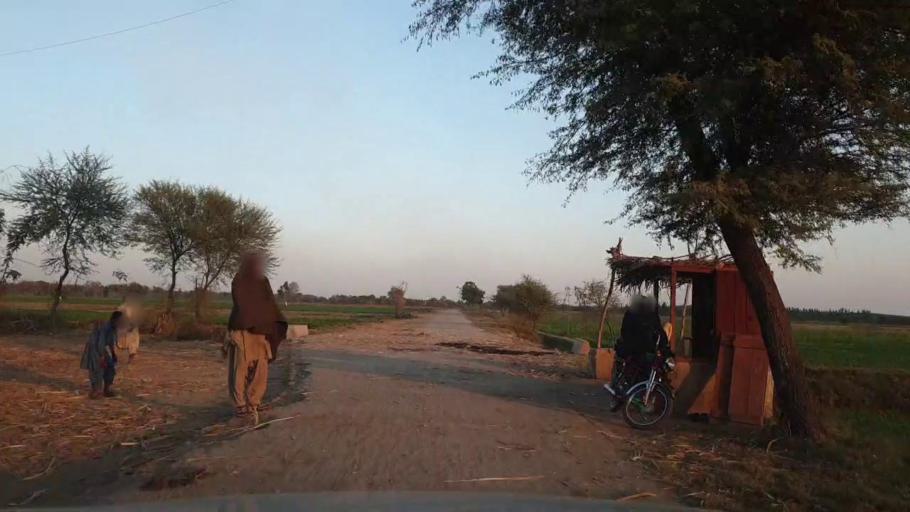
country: PK
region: Sindh
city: Tando Allahyar
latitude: 25.5564
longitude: 68.6402
